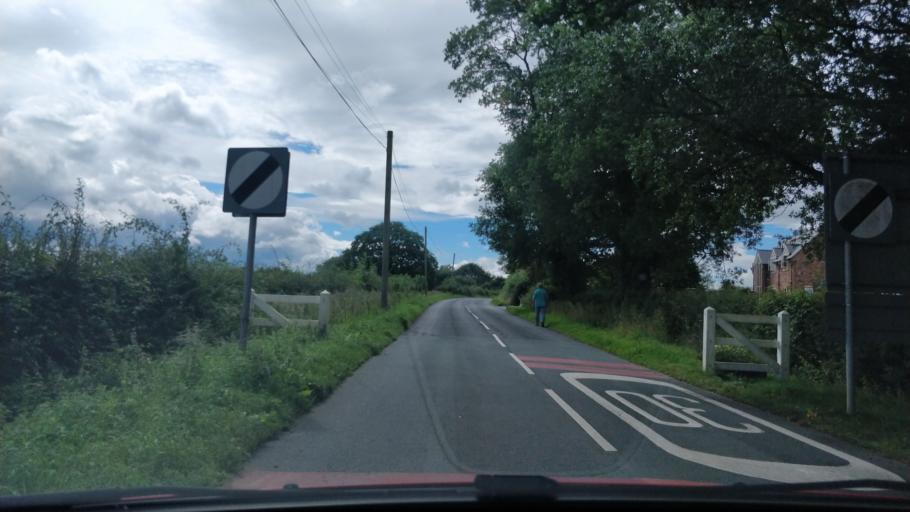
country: GB
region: Wales
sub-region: County of Flintshire
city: Hope
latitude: 53.1393
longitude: -3.0089
